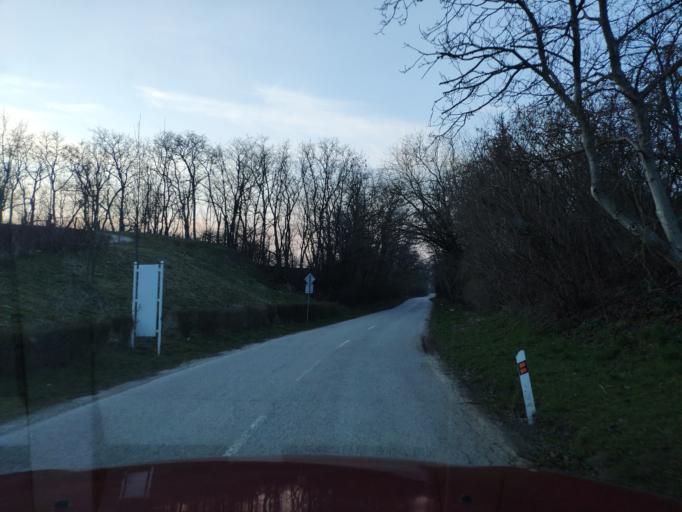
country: SK
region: Trnavsky
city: Leopoldov
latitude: 48.4677
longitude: 17.7184
